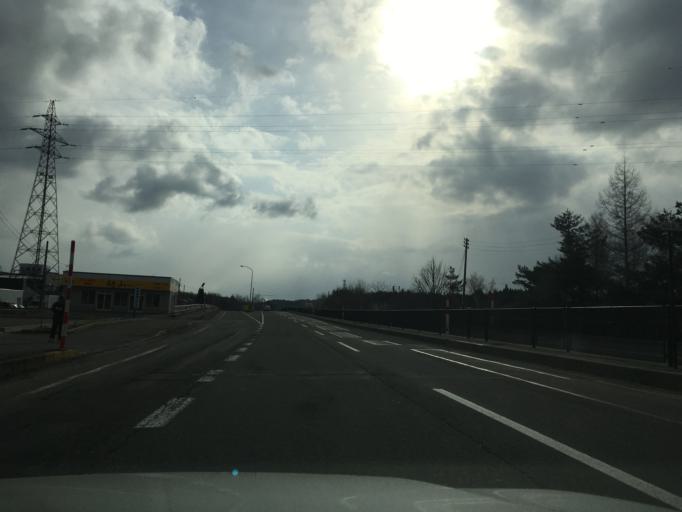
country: JP
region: Aomori
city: Aomori Shi
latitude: 40.8307
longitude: 140.6616
